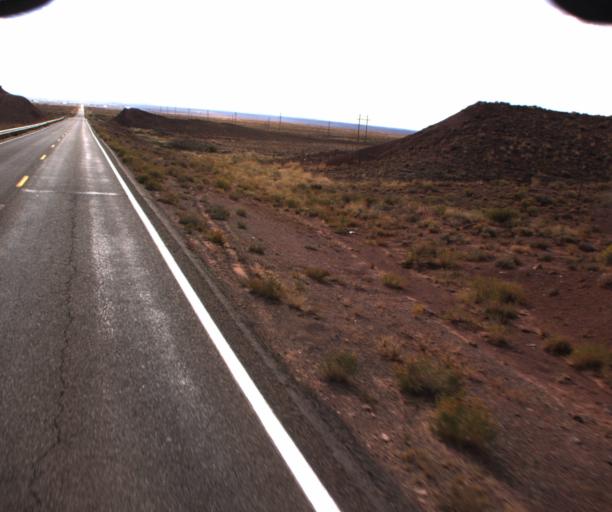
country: US
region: Arizona
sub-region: Apache County
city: Many Farms
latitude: 36.5391
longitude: -109.5205
